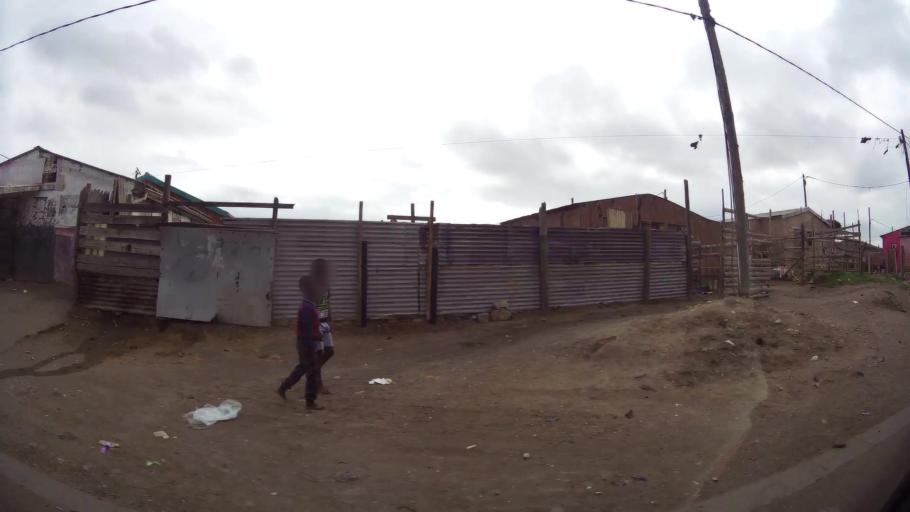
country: ZA
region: Eastern Cape
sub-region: Nelson Mandela Bay Metropolitan Municipality
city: Port Elizabeth
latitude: -33.8868
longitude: 25.5536
